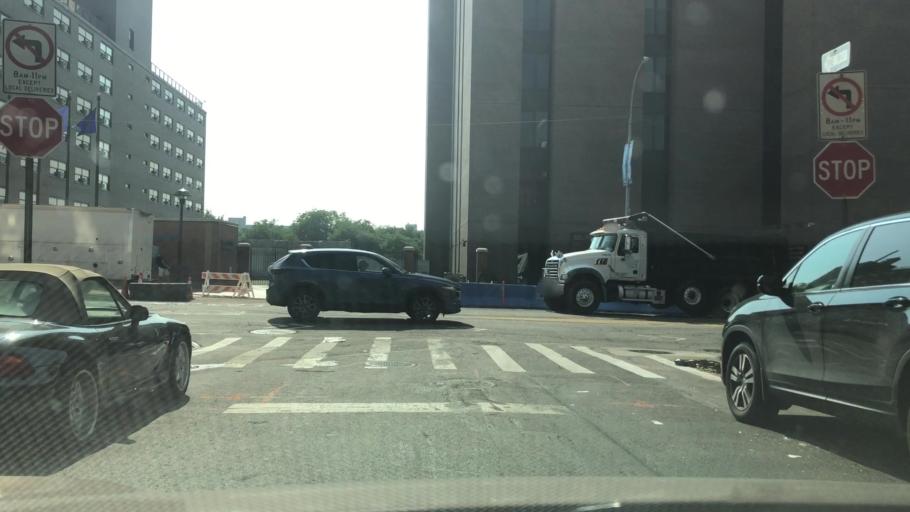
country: US
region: New York
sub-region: New York County
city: Inwood
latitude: 40.8500
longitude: -73.9299
